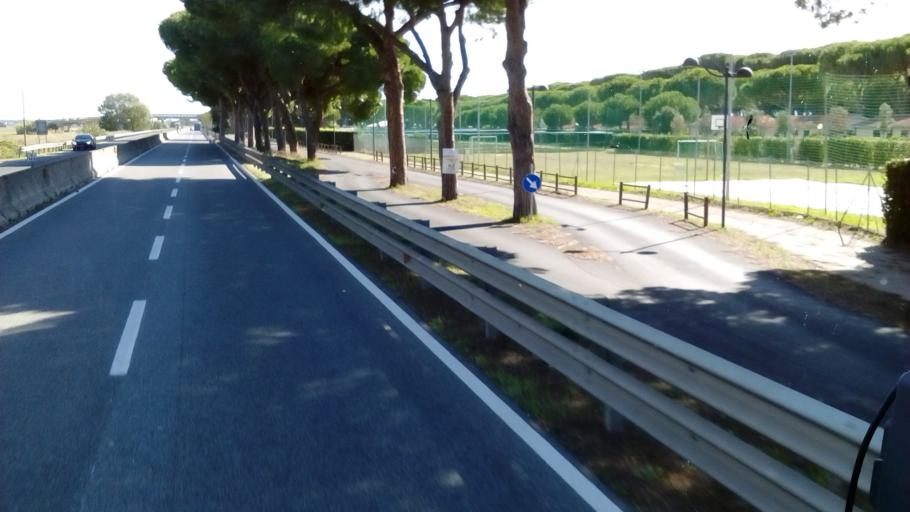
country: IT
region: Tuscany
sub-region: Provincia di Grosseto
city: Albinia
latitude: 42.5269
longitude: 11.1891
